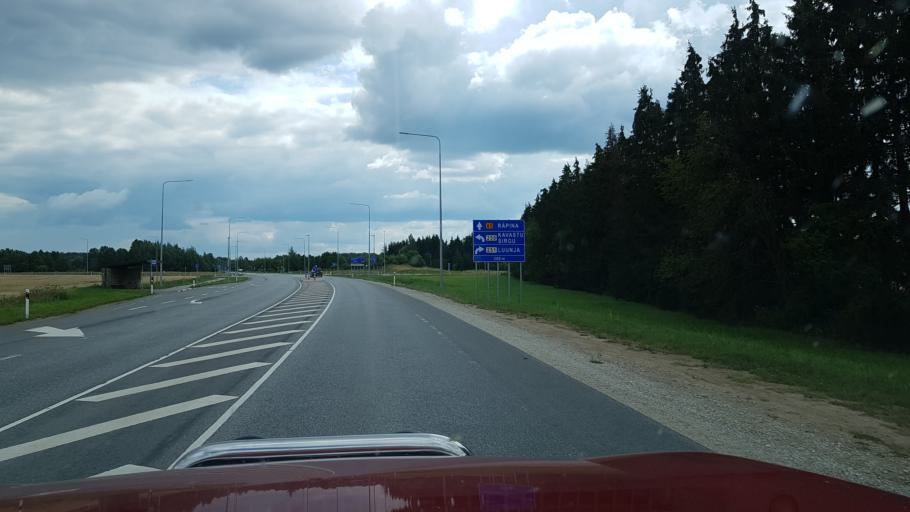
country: EE
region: Tartu
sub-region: Tartu linn
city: Tartu
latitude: 58.3622
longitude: 26.8902
